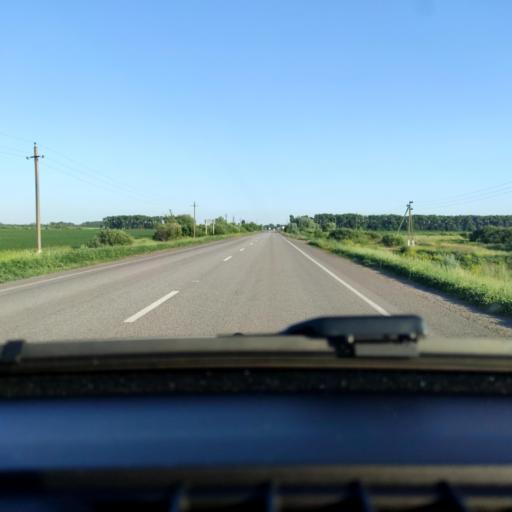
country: RU
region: Voronezj
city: Kashirskoye
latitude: 51.4742
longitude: 39.8605
